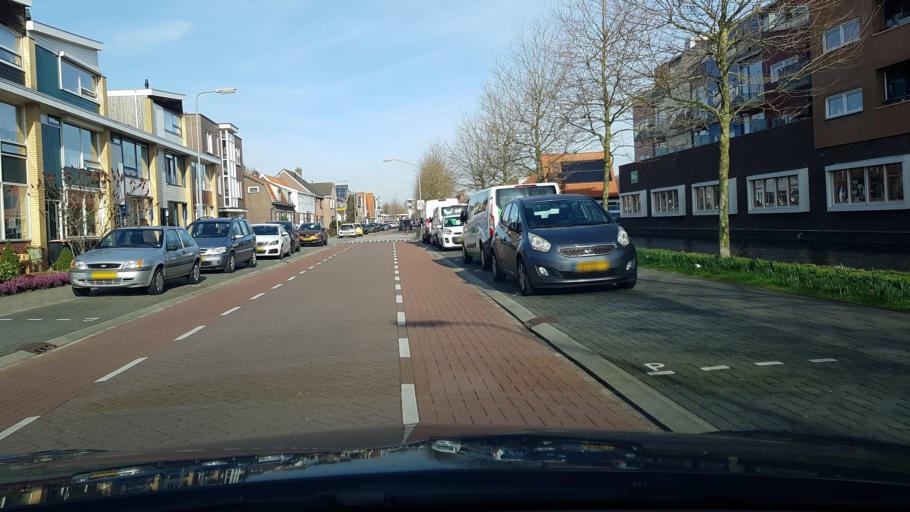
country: NL
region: North Holland
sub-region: Gemeente Zaanstad
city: Zaanstad
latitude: 52.4958
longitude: 4.8127
